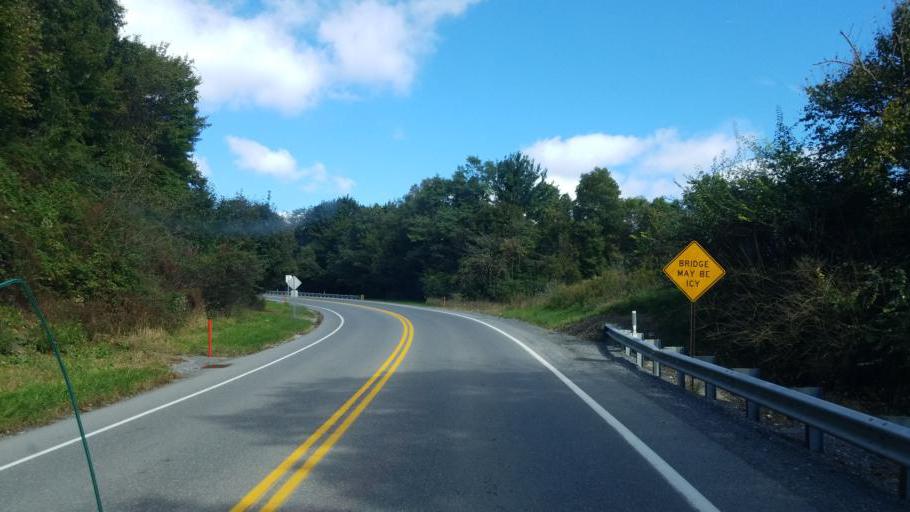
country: US
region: Pennsylvania
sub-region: Fulton County
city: McConnellsburg
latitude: 39.9362
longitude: -78.0158
